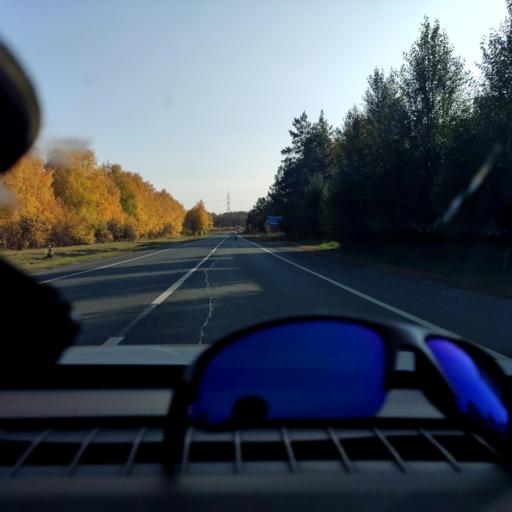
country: RU
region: Samara
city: Volzhskiy
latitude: 53.4549
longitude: 50.1263
